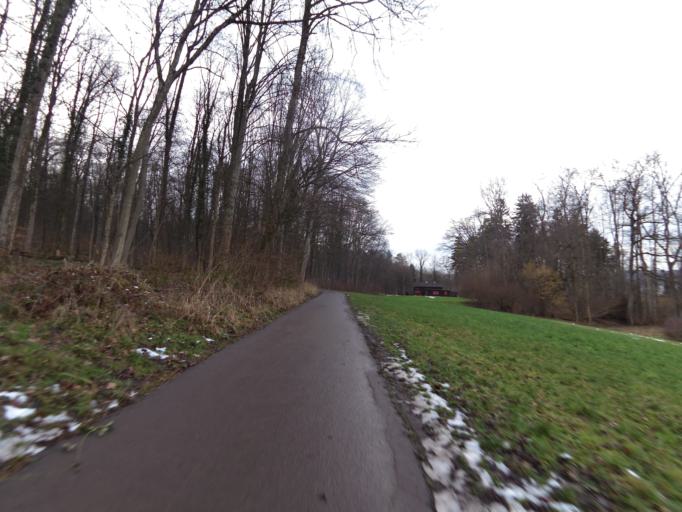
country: CH
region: Zurich
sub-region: Bezirk Zuerich
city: Zuerich (Kreis 9)
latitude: 47.3837
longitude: 8.4691
